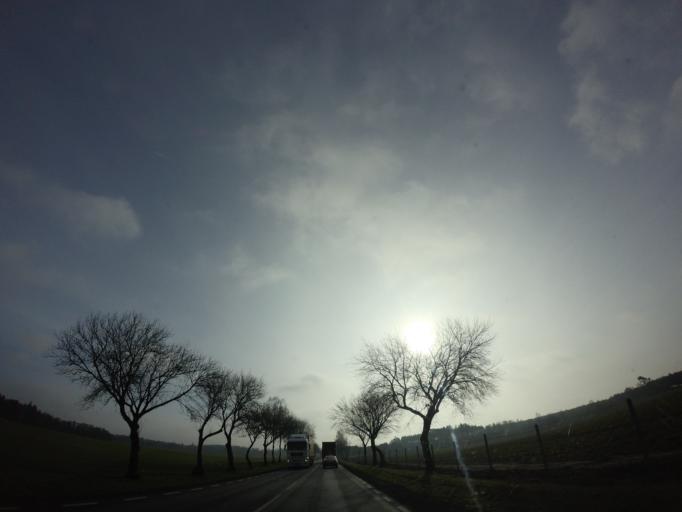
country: PL
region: West Pomeranian Voivodeship
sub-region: Powiat walecki
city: Walcz
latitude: 53.3182
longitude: 16.3287
